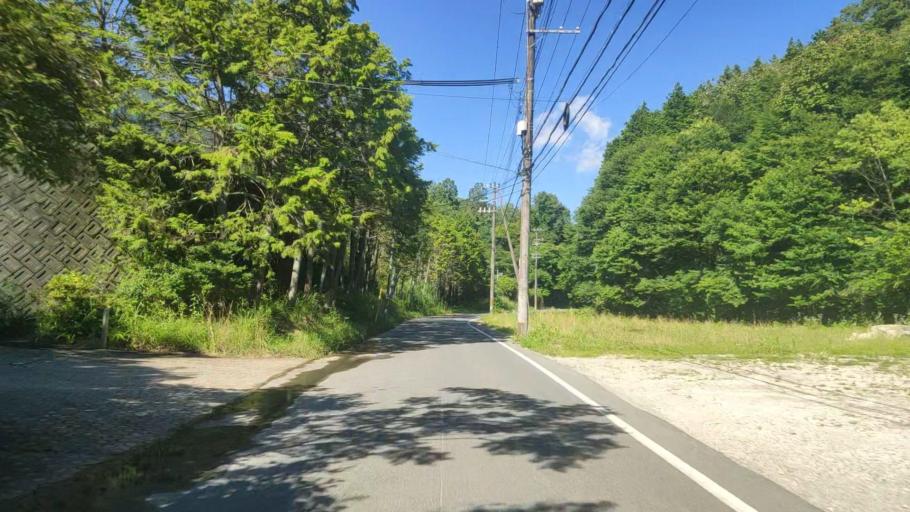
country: JP
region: Nara
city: Haibara-akanedai
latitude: 34.6174
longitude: 135.9749
